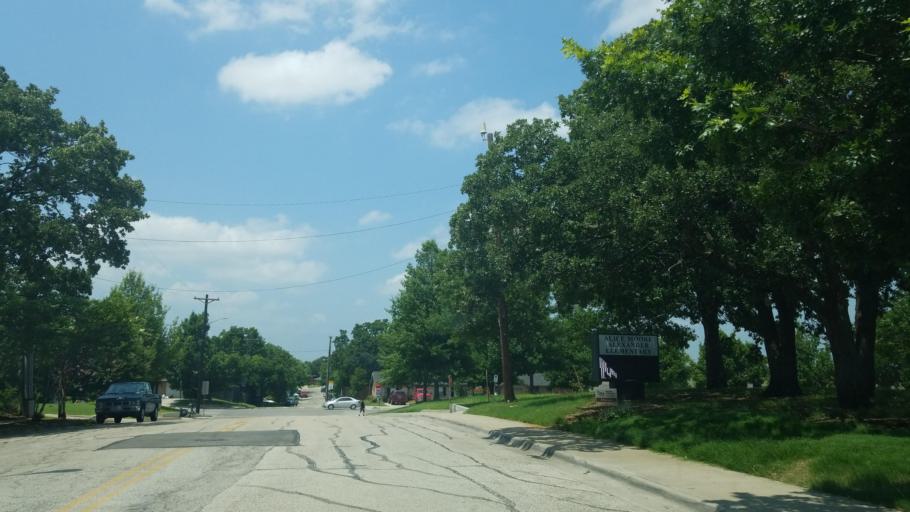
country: US
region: Texas
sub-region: Denton County
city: Denton
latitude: 33.2200
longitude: -97.1059
